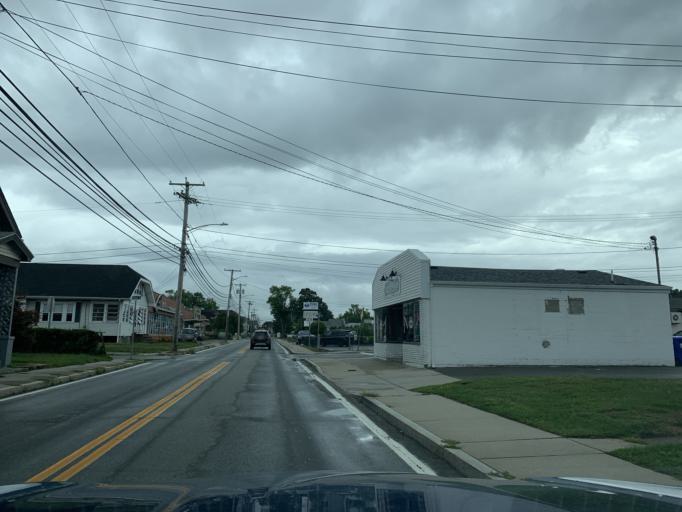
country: US
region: Rhode Island
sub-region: Bristol County
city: Warren
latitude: 41.7297
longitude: -71.2749
